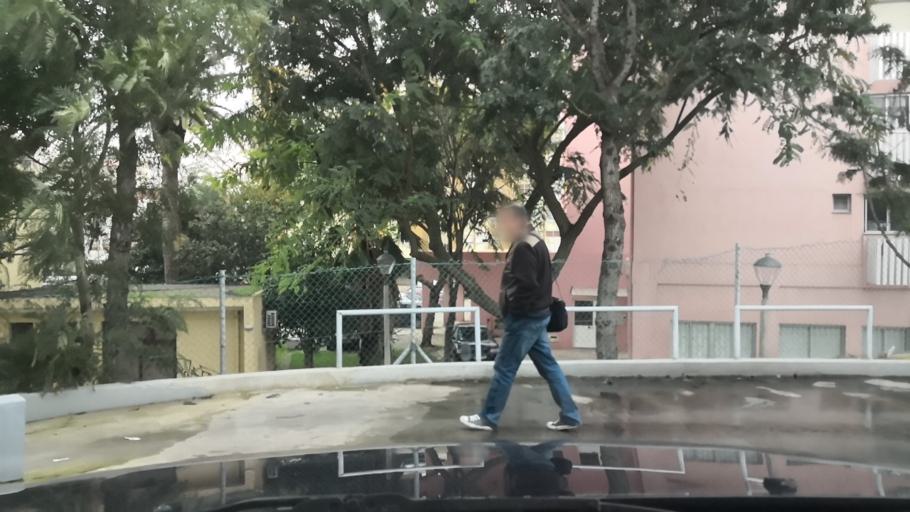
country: PT
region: Setubal
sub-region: Setubal
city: Setubal
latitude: 38.5325
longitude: -8.8870
